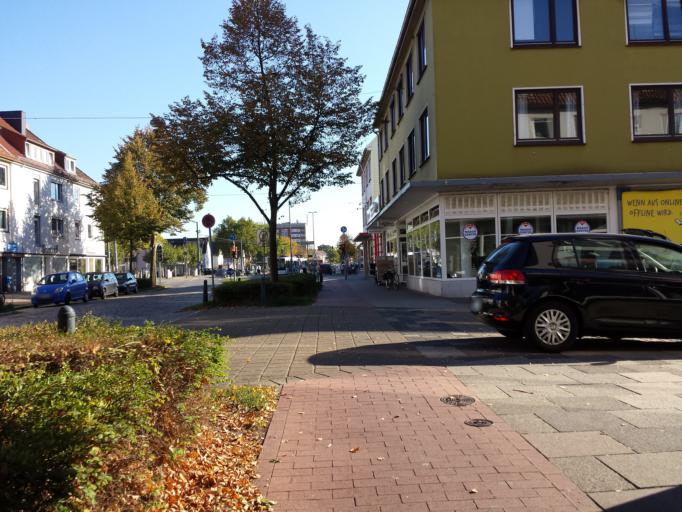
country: DE
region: Bremen
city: Bremen
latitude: 53.0944
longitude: 8.7878
